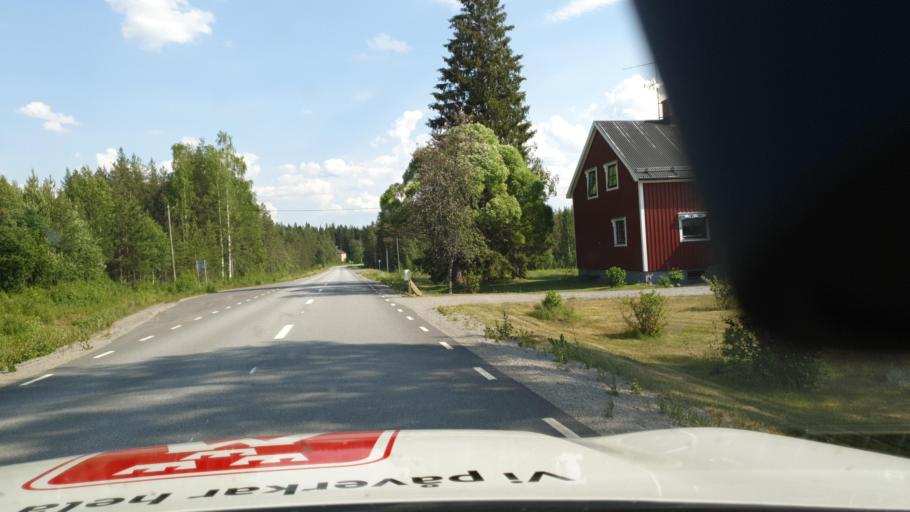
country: SE
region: Vaesterbotten
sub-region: Skelleftea Kommun
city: Forsbacka
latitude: 64.7288
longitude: 20.3998
